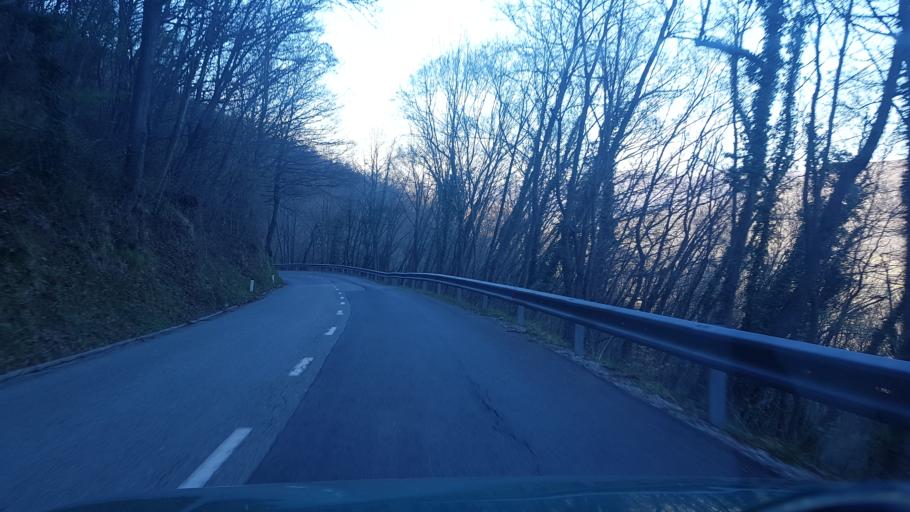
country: SI
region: Kanal
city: Deskle
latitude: 46.0268
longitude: 13.5770
